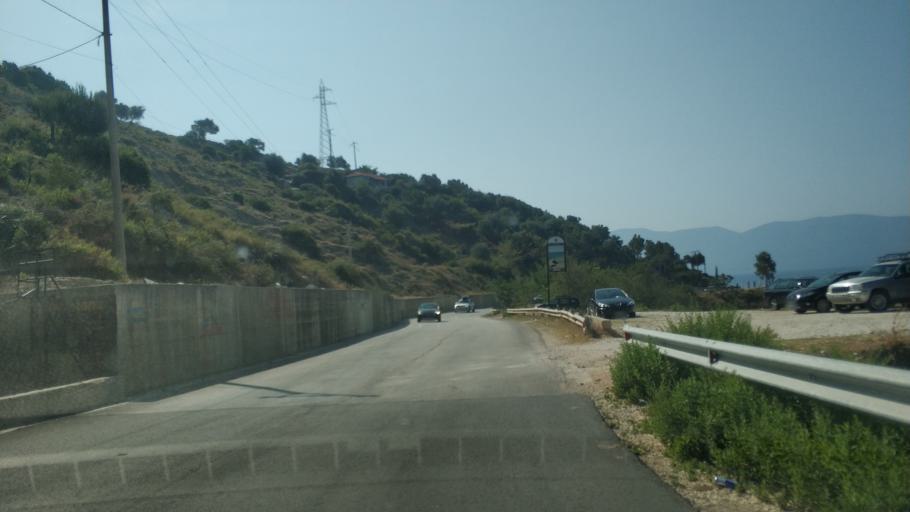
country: AL
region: Vlore
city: Vlore
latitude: 40.3974
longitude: 19.4793
